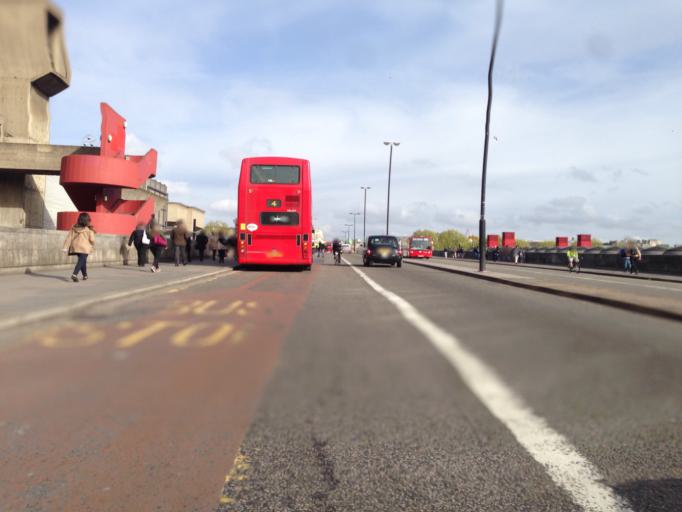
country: GB
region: England
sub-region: Greater London
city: City of Westminster
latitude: 51.5059
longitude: -0.1147
